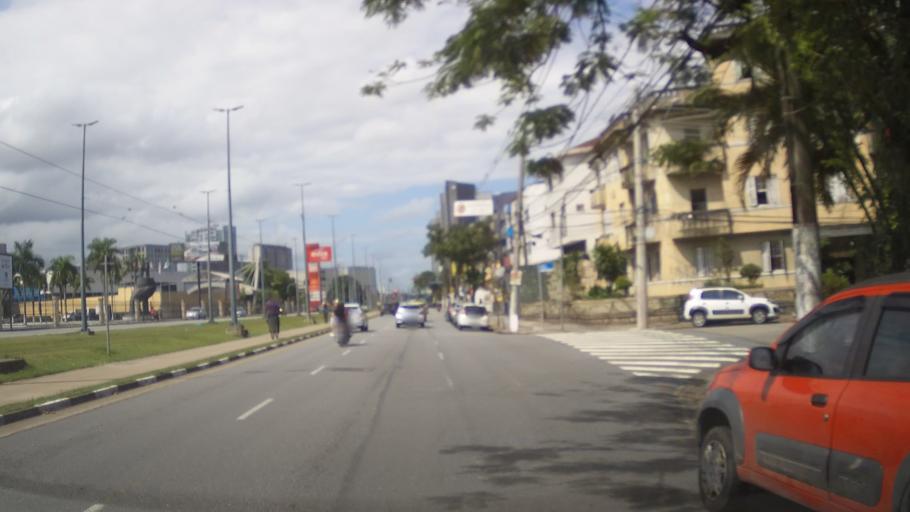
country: BR
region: Sao Paulo
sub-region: Santos
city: Santos
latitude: -23.9607
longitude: -46.3358
